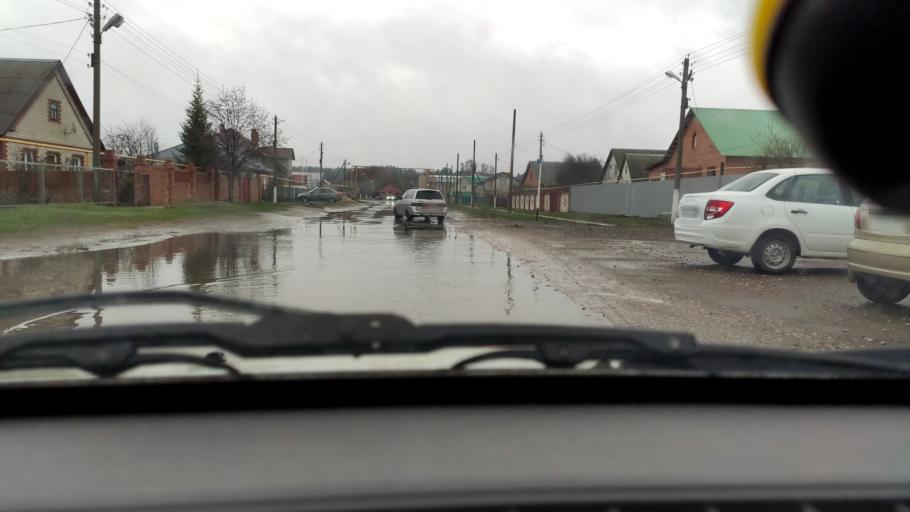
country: RU
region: Samara
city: Povolzhskiy
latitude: 53.6455
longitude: 49.6896
